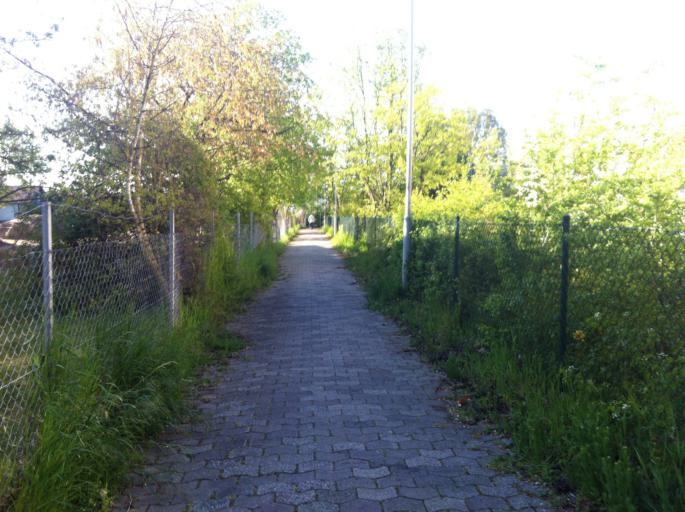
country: DE
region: Rheinland-Pfalz
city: Mainz
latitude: 50.0030
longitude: 8.2240
